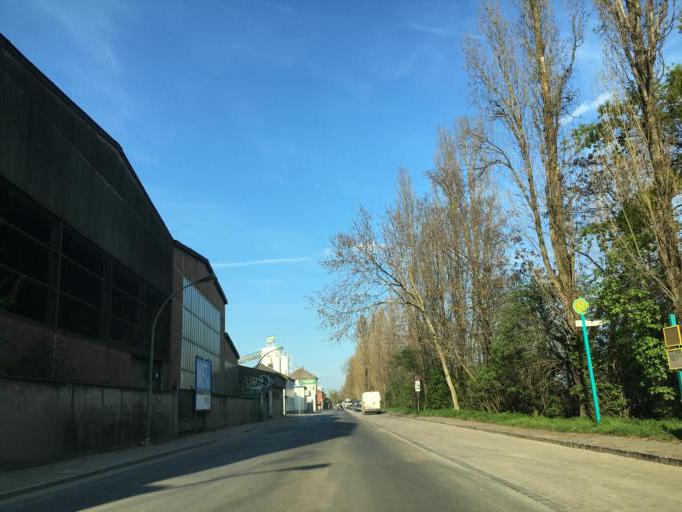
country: DE
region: Hesse
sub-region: Regierungsbezirk Darmstadt
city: Frankfurt am Main
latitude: 50.1092
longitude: 8.7237
